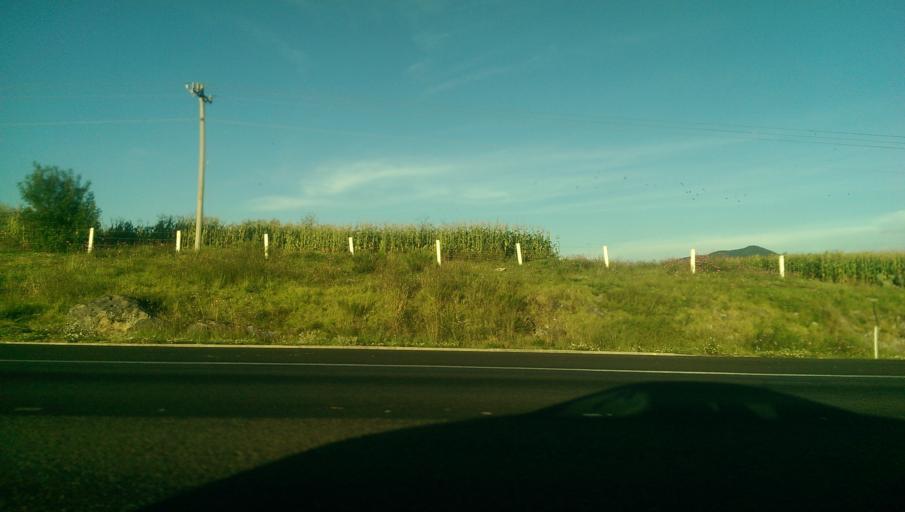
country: MX
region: Mexico
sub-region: Aculco
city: El Colorado
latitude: 20.1367
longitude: -99.7298
